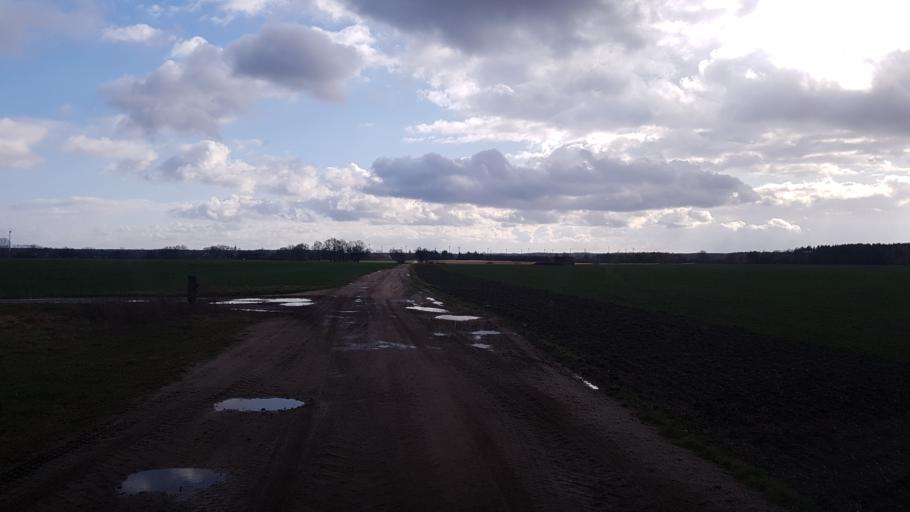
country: DE
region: Brandenburg
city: Sallgast
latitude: 51.6201
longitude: 13.8559
